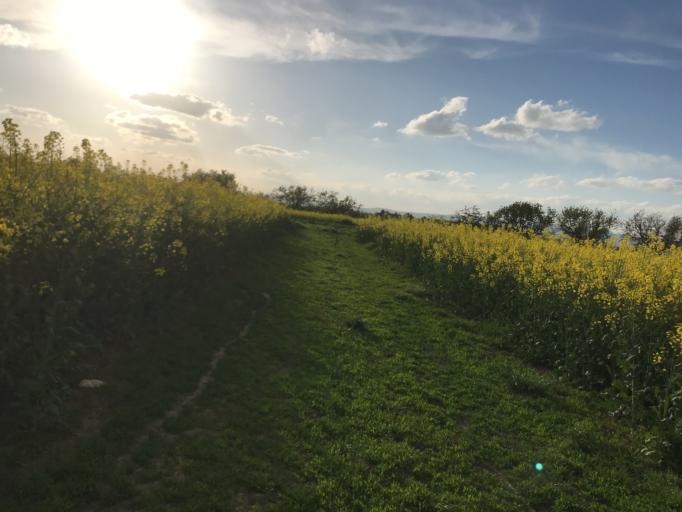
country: DE
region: Rheinland-Pfalz
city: Wackernheim
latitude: 49.9705
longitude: 8.1356
